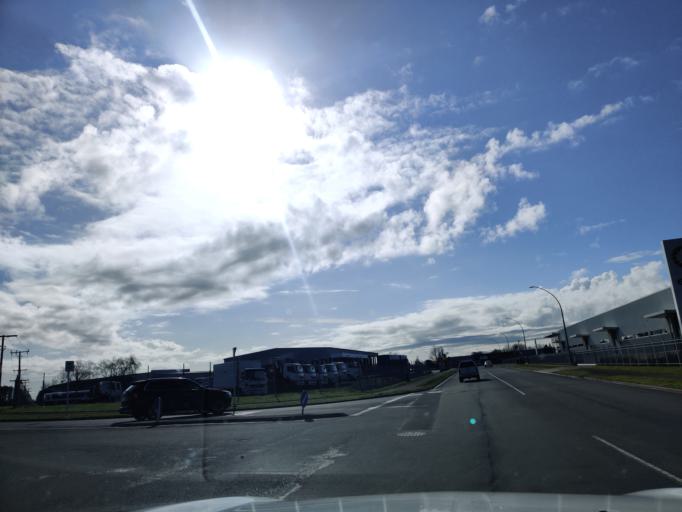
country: NZ
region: Waikato
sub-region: Hamilton City
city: Hamilton
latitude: -37.7305
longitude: 175.2170
